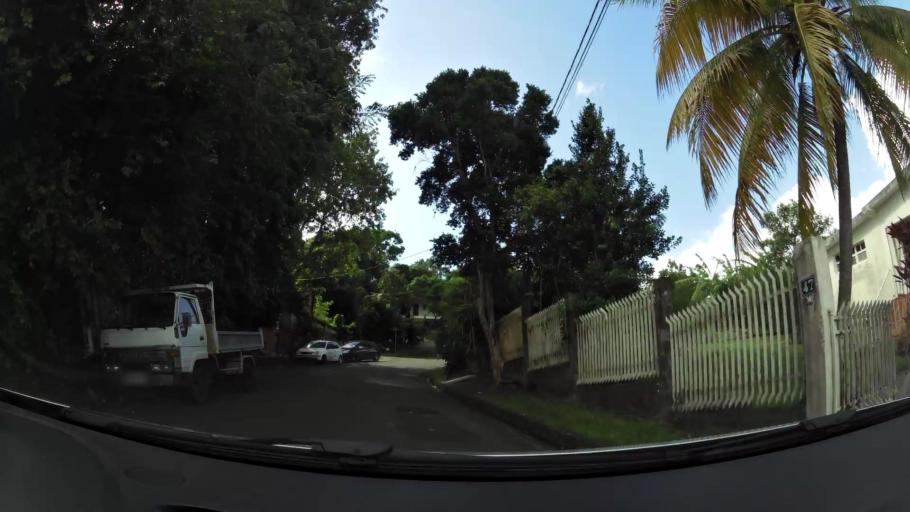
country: MQ
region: Martinique
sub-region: Martinique
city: Fort-de-France
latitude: 14.6334
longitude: -61.0482
